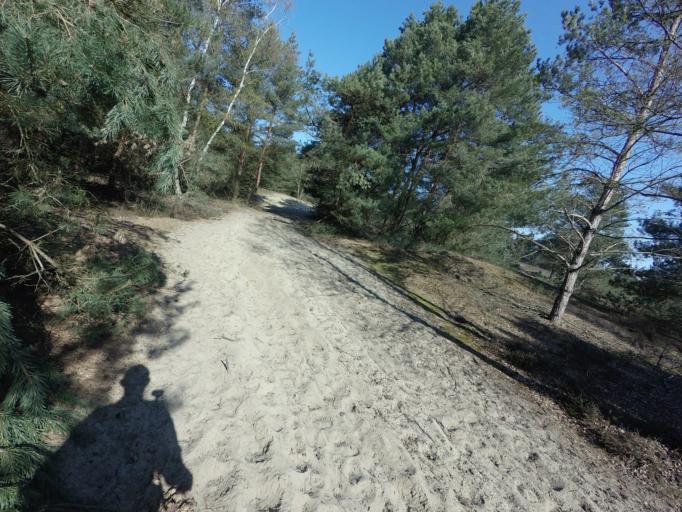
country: NL
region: Limburg
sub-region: Gemeente Bergen
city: Wellerlooi
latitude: 51.5899
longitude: 6.0856
